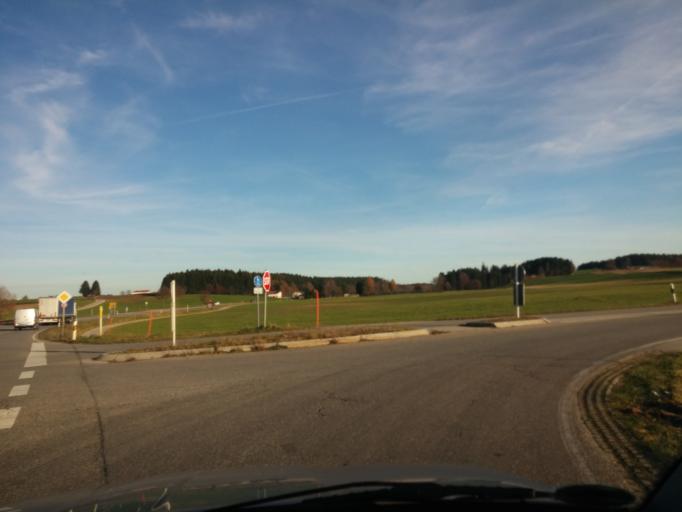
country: DE
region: Bavaria
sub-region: Upper Bavaria
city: Obing
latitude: 48.0009
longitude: 12.4218
